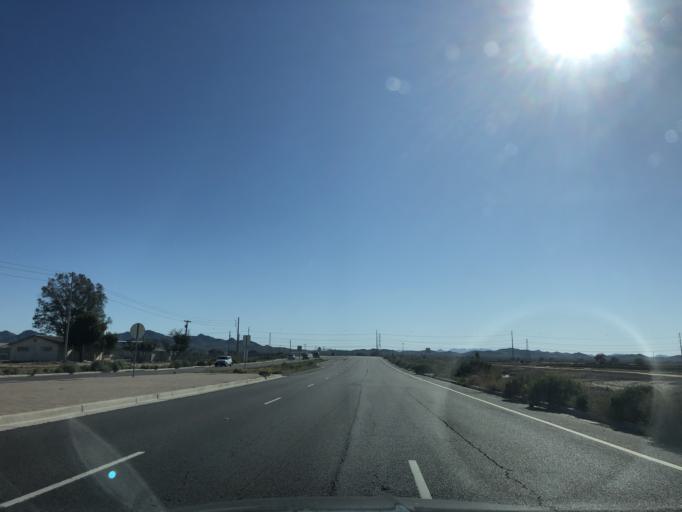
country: US
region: Arizona
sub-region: Maricopa County
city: Goodyear
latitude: 33.4033
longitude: -112.4269
